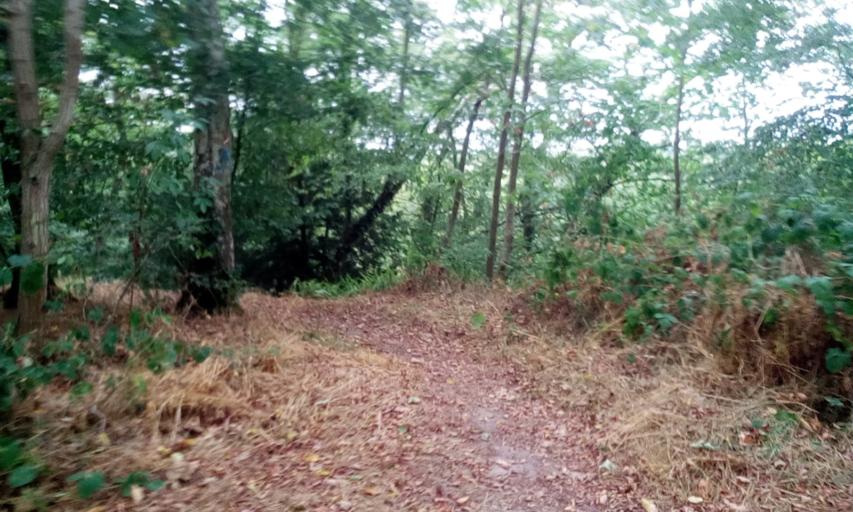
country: FR
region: Lower Normandy
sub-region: Departement du Calvados
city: Mouen
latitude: 49.1352
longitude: -0.4837
